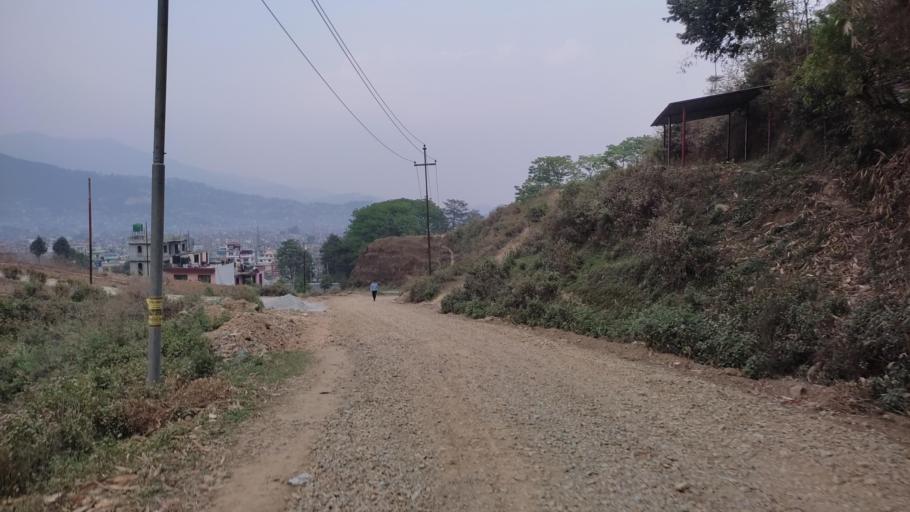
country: NP
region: Central Region
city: Kirtipur
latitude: 27.6742
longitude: 85.2399
